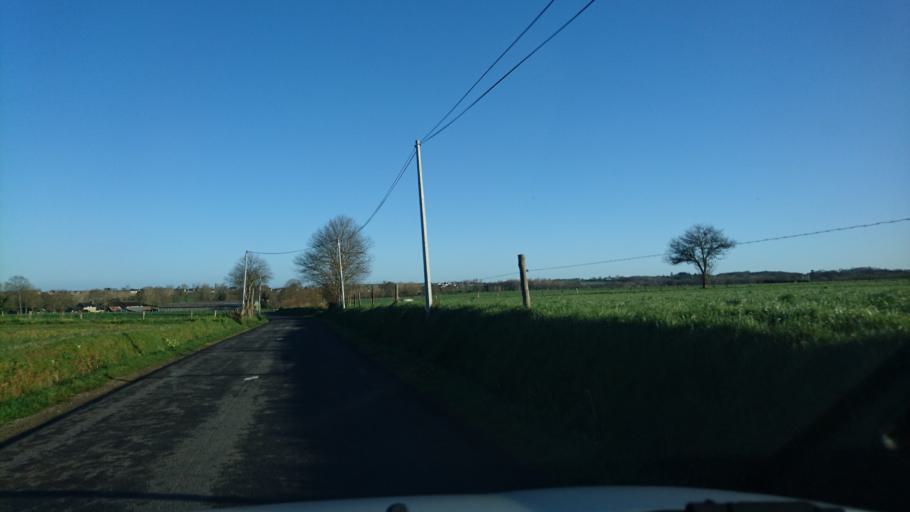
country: FR
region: Brittany
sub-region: Departement d'Ille-et-Vilaine
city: Baguer-Pican
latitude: 48.5413
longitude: -1.6918
